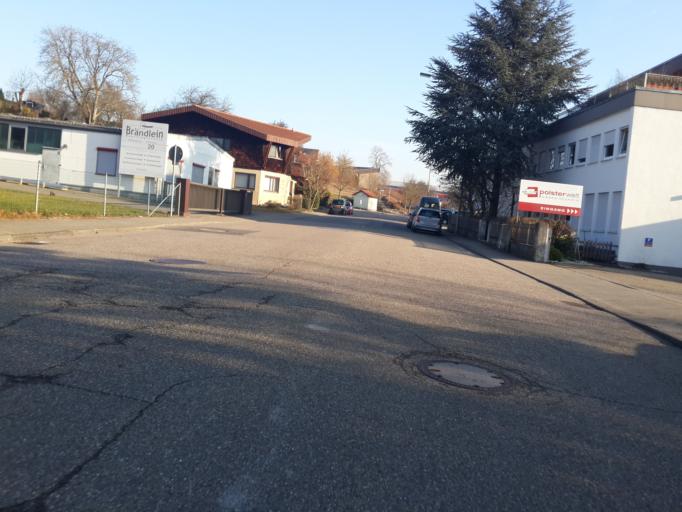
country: DE
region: Baden-Wuerttemberg
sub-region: Regierungsbezirk Stuttgart
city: Untereisesheim
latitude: 49.1966
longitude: 9.2047
